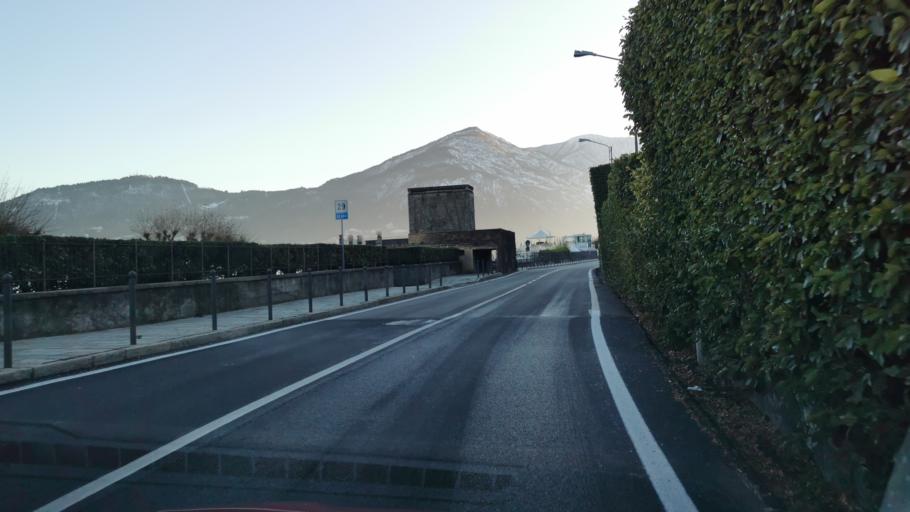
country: IT
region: Lombardy
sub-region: Provincia di Como
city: Griante
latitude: 45.9946
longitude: 9.2392
